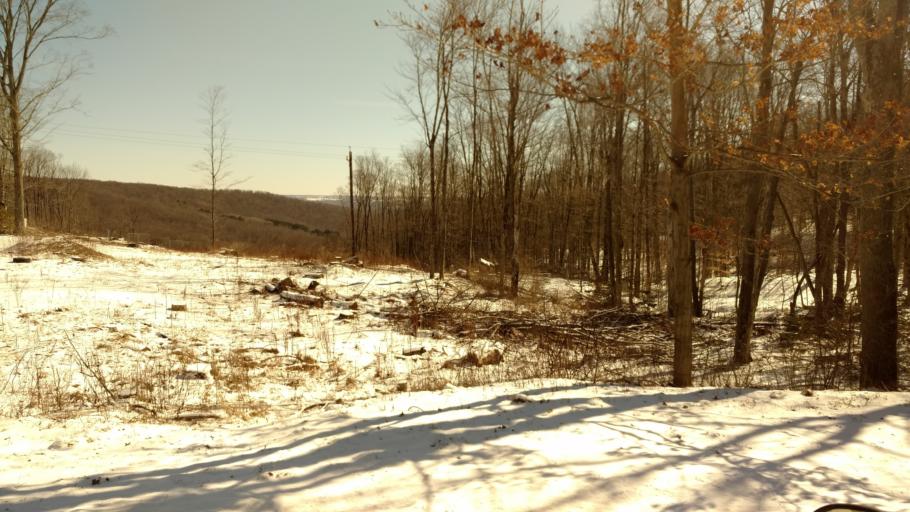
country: US
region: New York
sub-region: Allegany County
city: Wellsville
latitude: 42.0530
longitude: -78.0101
